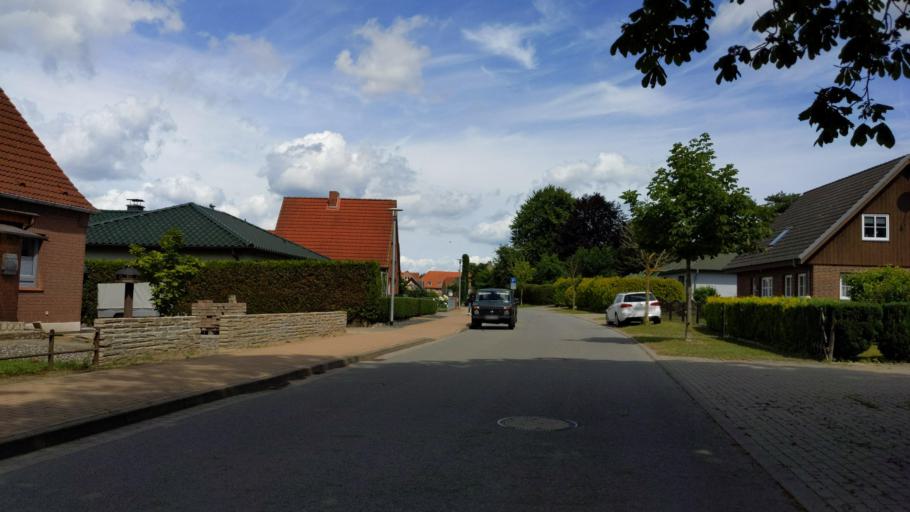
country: DE
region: Mecklenburg-Vorpommern
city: Dassow
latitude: 53.9052
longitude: 10.9758
